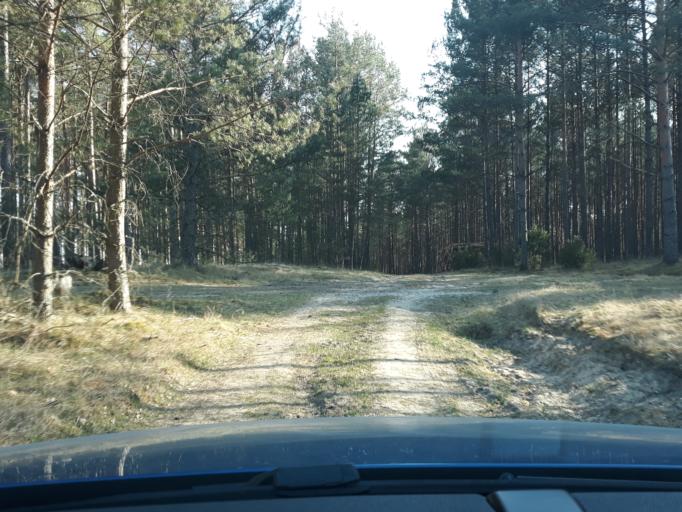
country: PL
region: Pomeranian Voivodeship
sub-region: Powiat bytowski
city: Lipnica
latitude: 53.9120
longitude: 17.4972
